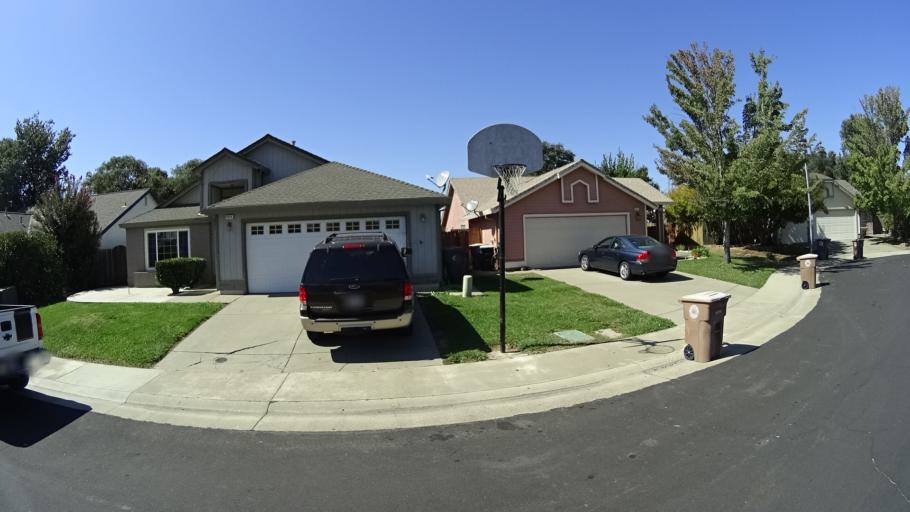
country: US
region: California
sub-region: Sacramento County
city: Laguna
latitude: 38.4373
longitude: -121.4310
